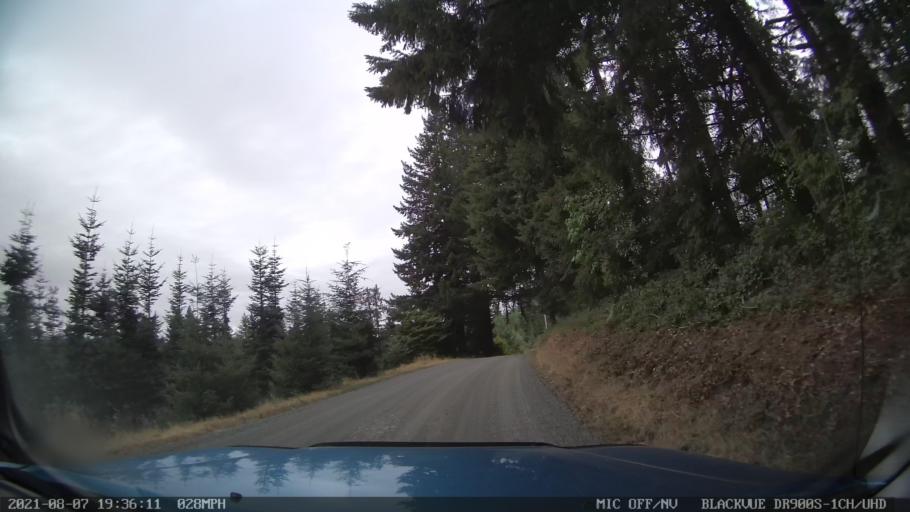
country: US
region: Oregon
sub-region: Marion County
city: Silverton
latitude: 44.9317
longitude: -122.6573
